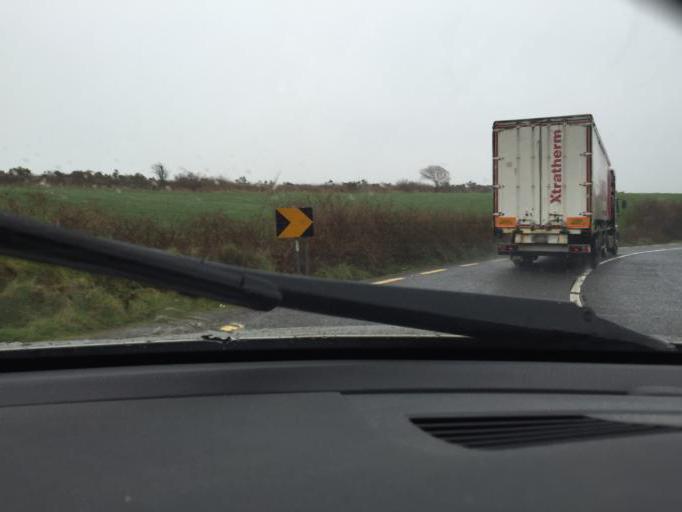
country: IE
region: Munster
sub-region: Ciarrai
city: Dingle
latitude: 52.1455
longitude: -10.1007
